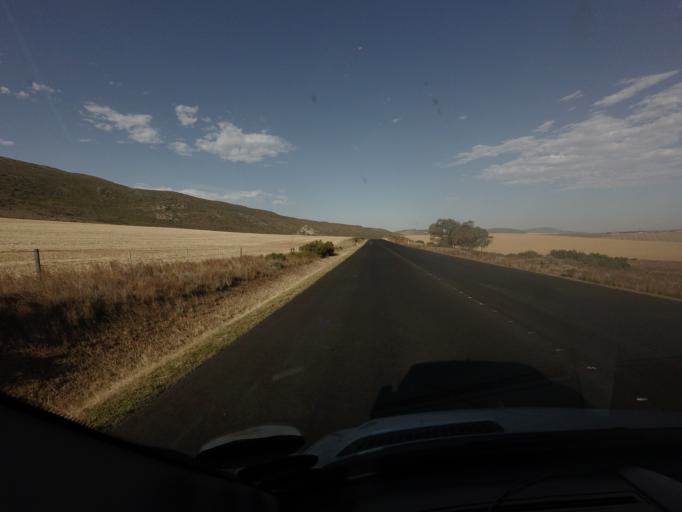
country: ZA
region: Western Cape
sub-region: Overberg District Municipality
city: Swellendam
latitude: -34.1012
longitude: 20.2004
